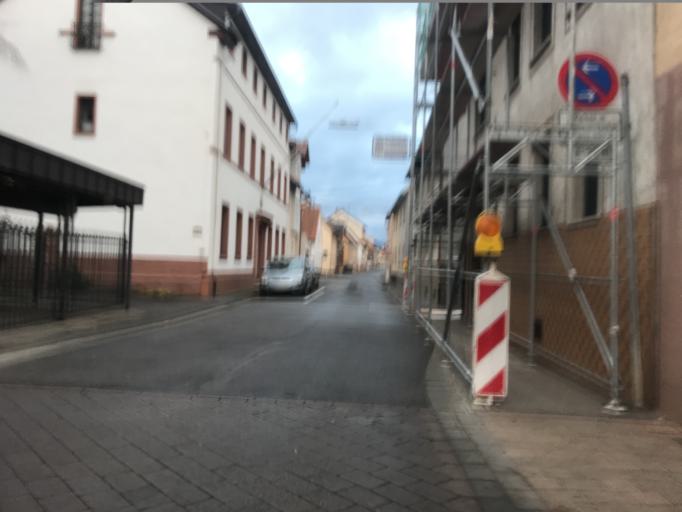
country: DE
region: Hesse
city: Geisenheim
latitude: 49.9664
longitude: 7.9598
